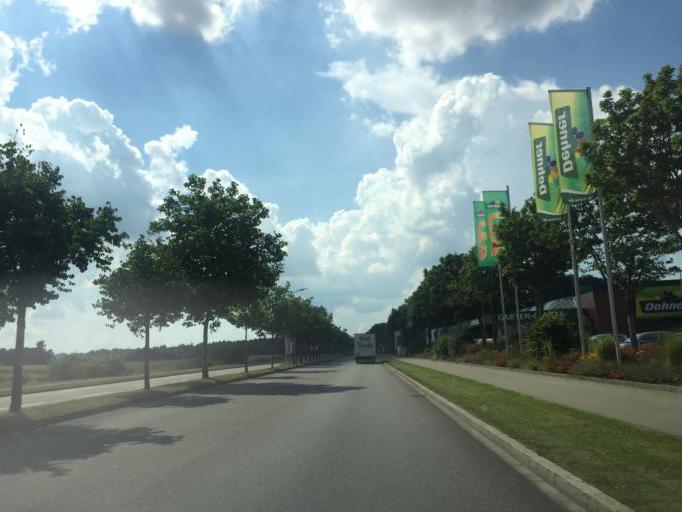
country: DE
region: Baden-Wuerttemberg
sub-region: Freiburg Region
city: Singen
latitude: 47.7523
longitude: 8.8818
